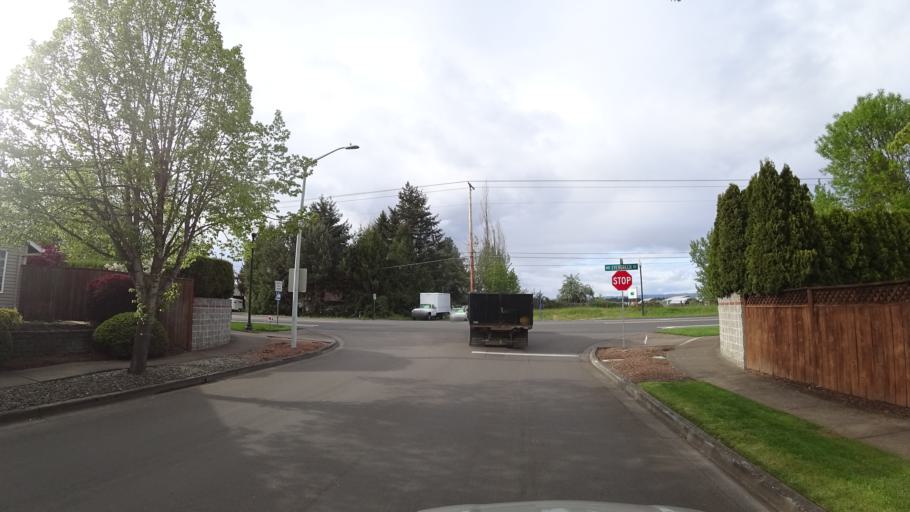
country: US
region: Oregon
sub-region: Washington County
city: Hillsboro
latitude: 45.5497
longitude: -122.9694
